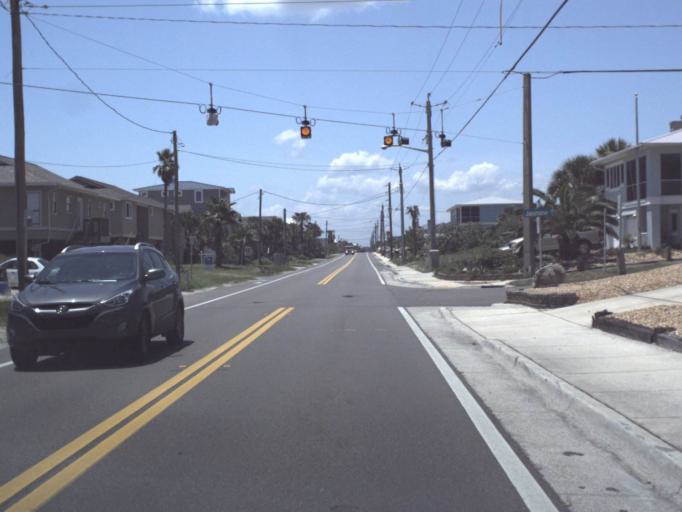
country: US
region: Florida
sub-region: Nassau County
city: Fernandina Beach
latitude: 30.6558
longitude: -81.4332
